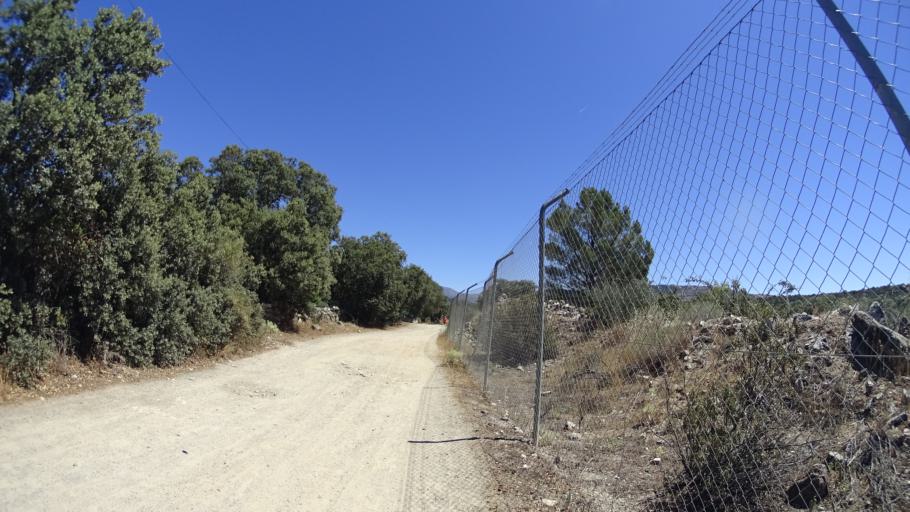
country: ES
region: Madrid
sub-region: Provincia de Madrid
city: Alpedrete
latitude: 40.6707
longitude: -4.0433
